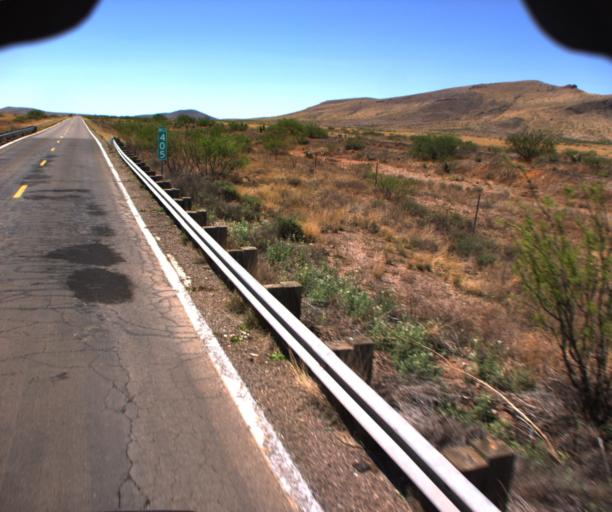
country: US
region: Arizona
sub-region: Cochise County
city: Douglas
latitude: 31.6817
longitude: -109.1390
